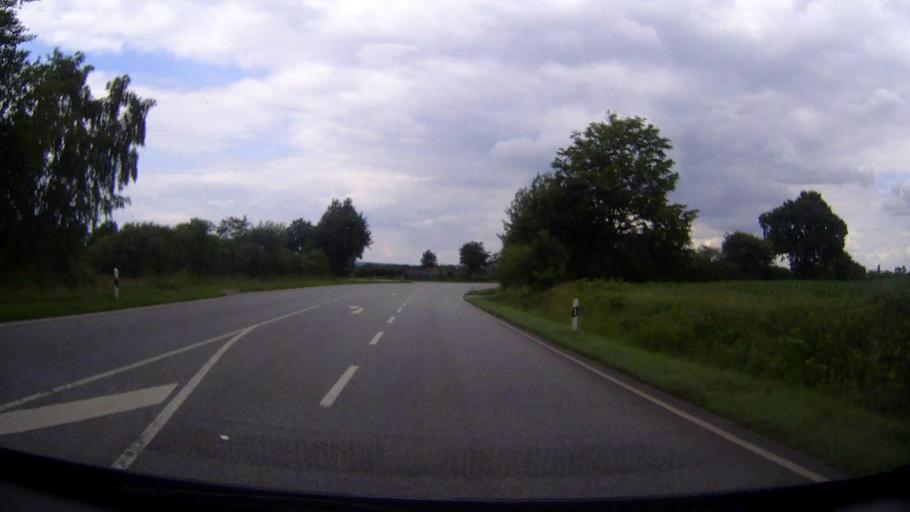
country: DE
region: Schleswig-Holstein
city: Reher
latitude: 54.0749
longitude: 9.5793
